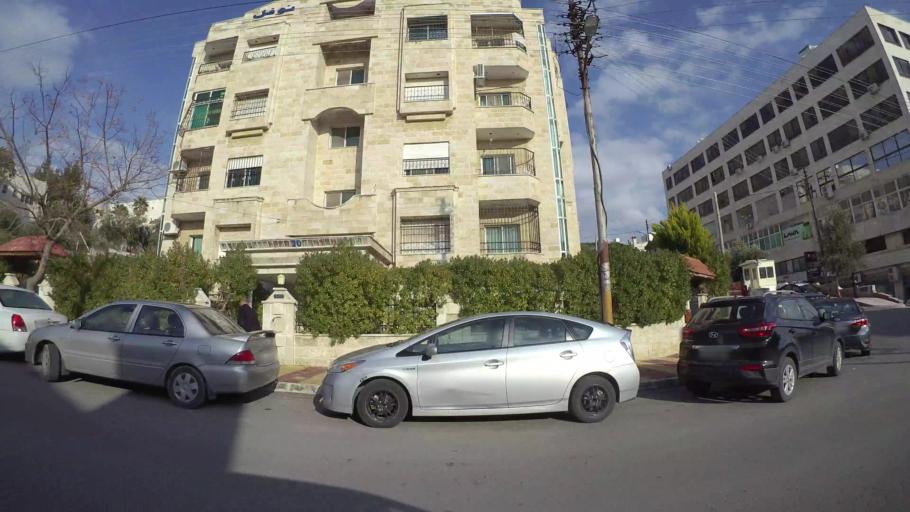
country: JO
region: Amman
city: Al Jubayhah
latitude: 31.9825
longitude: 35.8756
